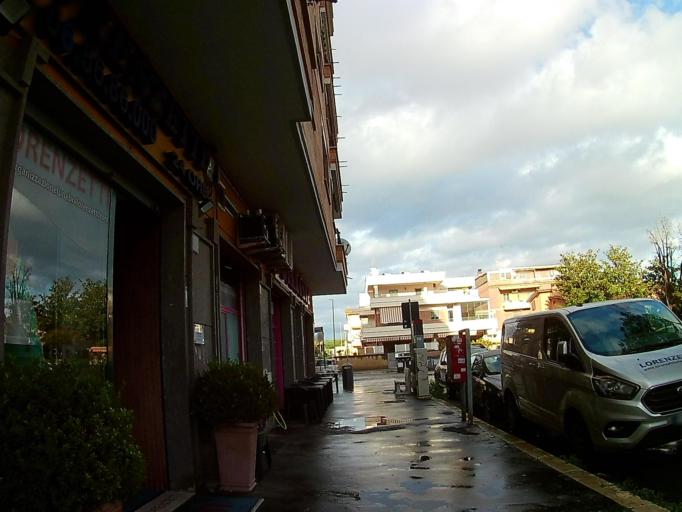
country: IT
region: Latium
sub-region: Citta metropolitana di Roma Capitale
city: Lido di Ostia
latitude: 41.7378
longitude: 12.2889
